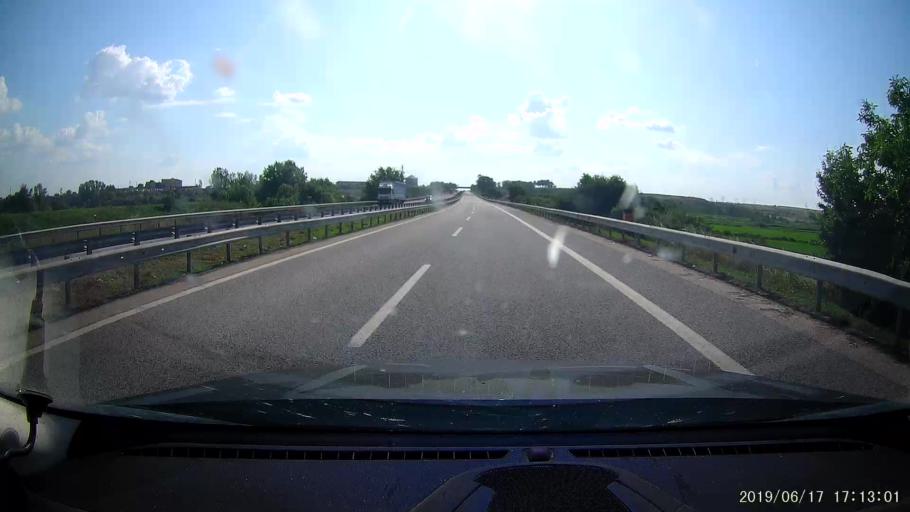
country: TR
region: Edirne
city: Edirne
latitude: 41.7013
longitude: 26.5490
